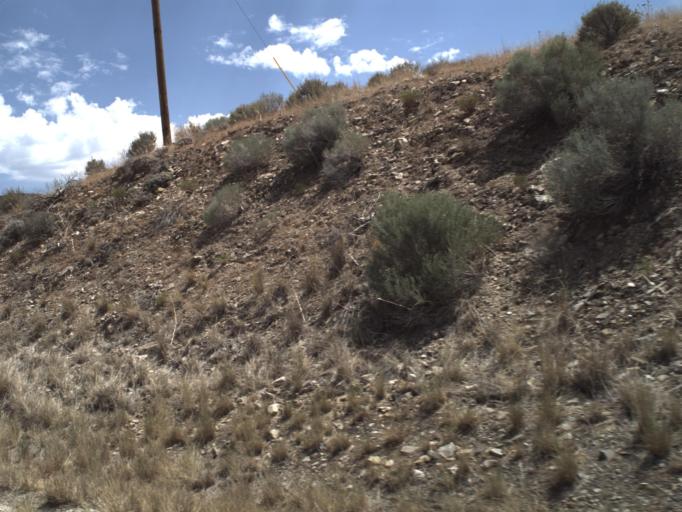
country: US
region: Utah
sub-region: Tooele County
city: Tooele
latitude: 40.4616
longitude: -112.3560
